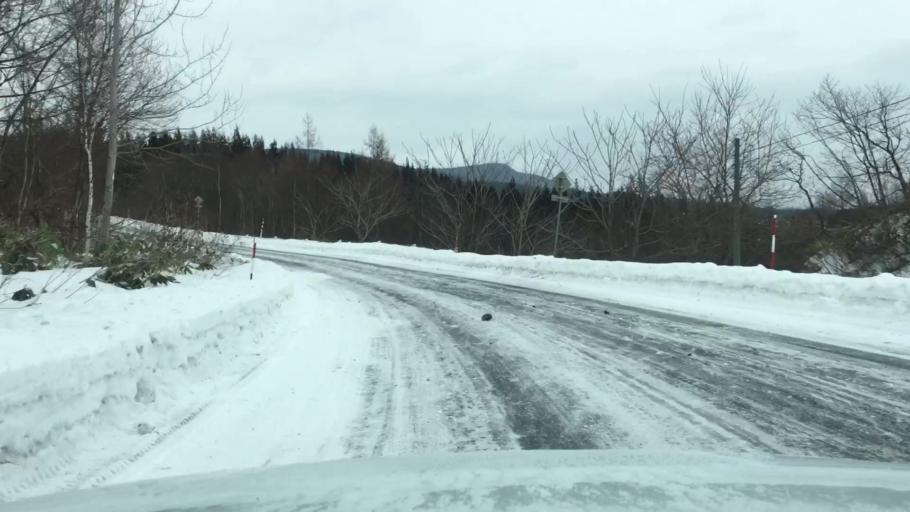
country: JP
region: Iwate
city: Shizukuishi
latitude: 39.9364
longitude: 141.0021
